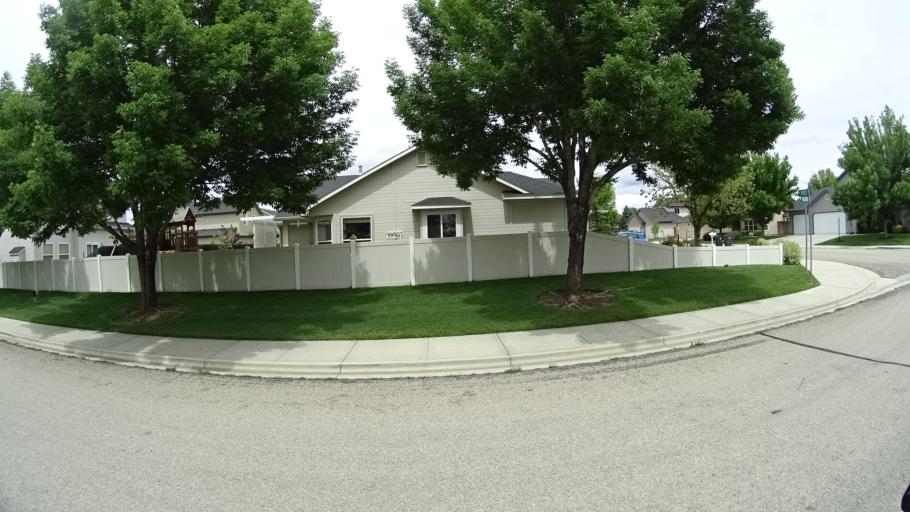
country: US
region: Idaho
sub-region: Ada County
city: Meridian
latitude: 43.6375
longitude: -116.3974
